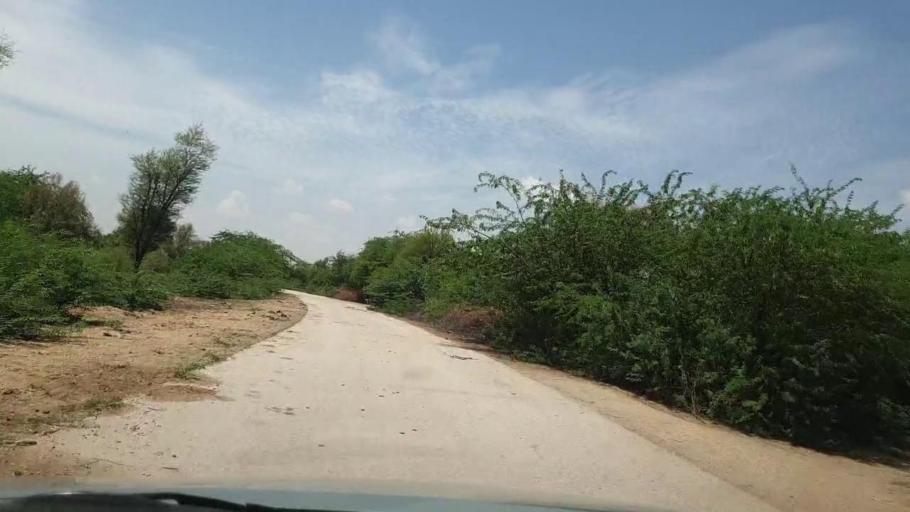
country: PK
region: Sindh
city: Bozdar
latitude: 27.0235
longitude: 68.9332
